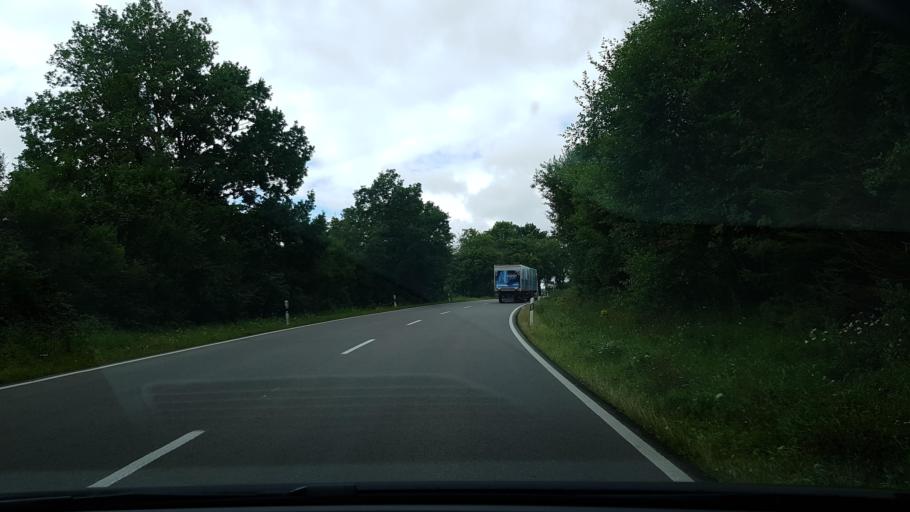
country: DE
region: Baden-Wuerttemberg
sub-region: Tuebingen Region
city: Laichingen
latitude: 48.4632
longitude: 9.6598
